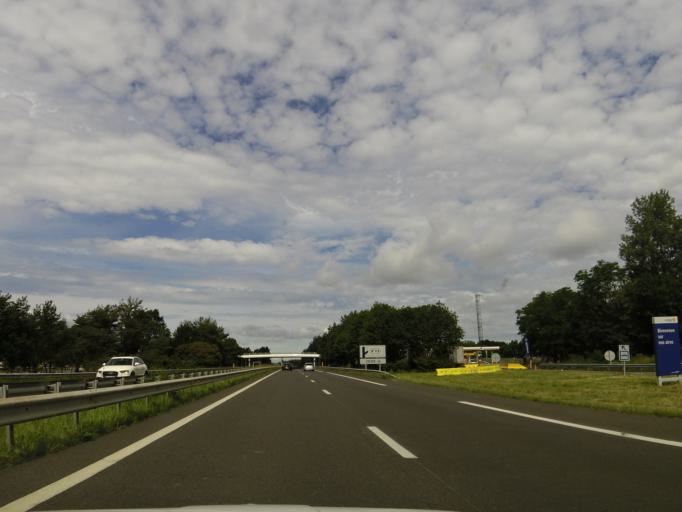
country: FR
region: Auvergne
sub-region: Departement du Puy-de-Dome
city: Orleat
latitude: 45.8514
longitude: 3.4076
